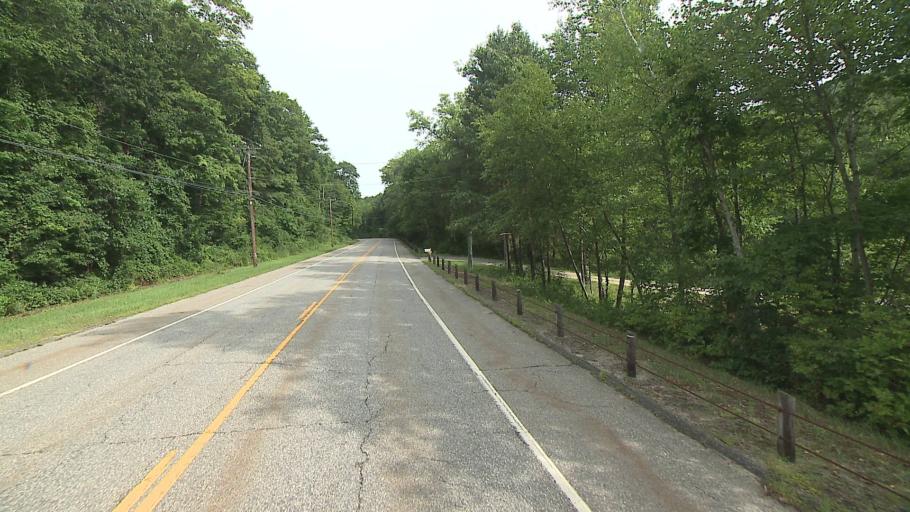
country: US
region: Connecticut
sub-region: Litchfield County
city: New Preston
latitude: 41.6732
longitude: -73.3248
